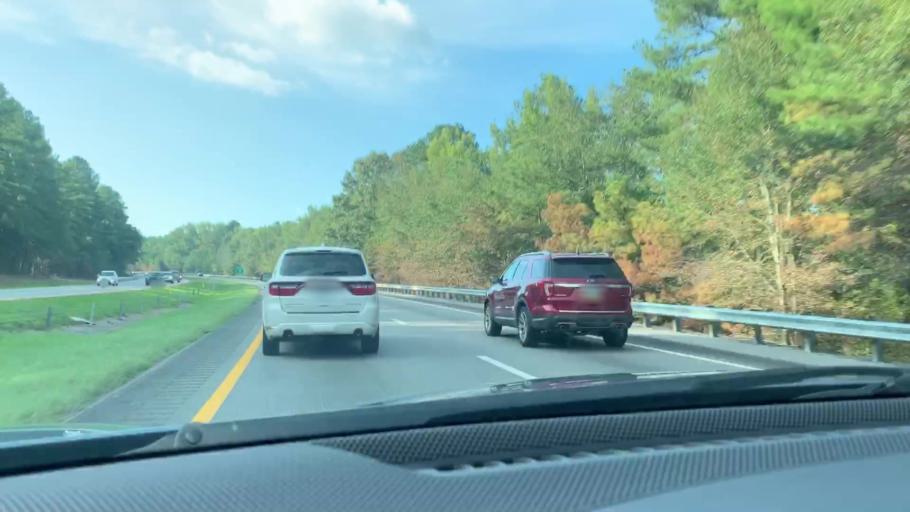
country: US
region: South Carolina
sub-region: Calhoun County
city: Oak Grove
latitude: 33.7536
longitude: -80.9456
